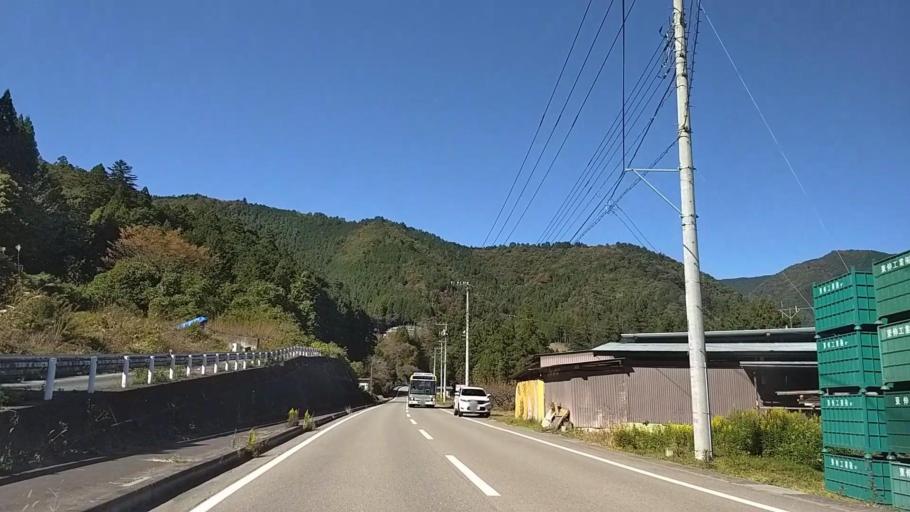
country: JP
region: Yamanashi
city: Uenohara
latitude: 35.6620
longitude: 139.0893
